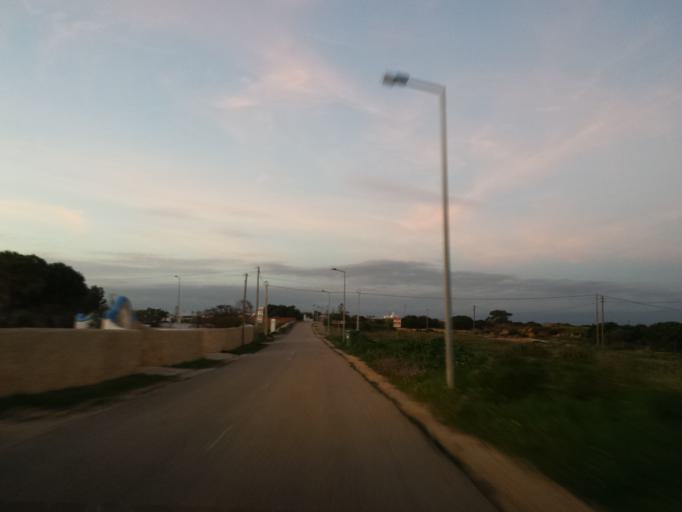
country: PT
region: Faro
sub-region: Lagos
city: Lagos
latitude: 37.0857
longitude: -8.6709
